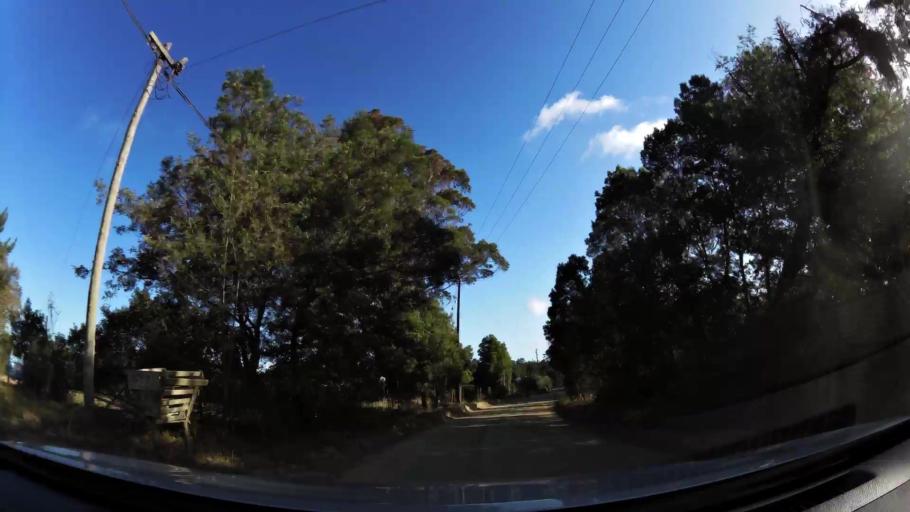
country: ZA
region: Western Cape
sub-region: Eden District Municipality
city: George
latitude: -33.9797
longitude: 22.5728
